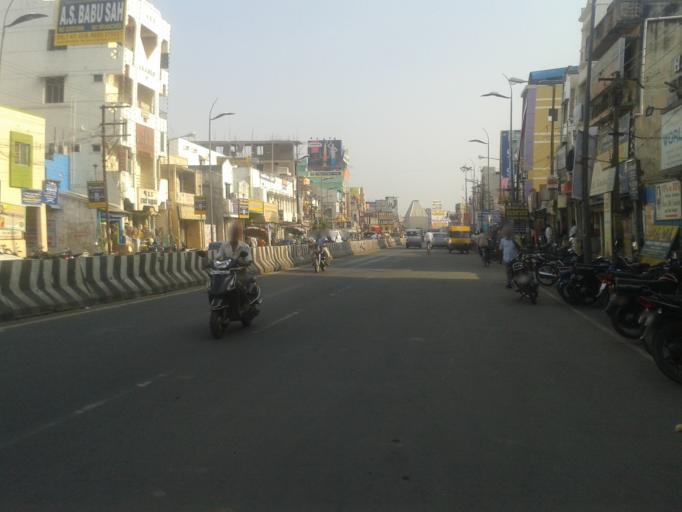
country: IN
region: Tamil Nadu
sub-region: Kancheepuram
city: Kanchipuram
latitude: 12.8280
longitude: 79.7073
